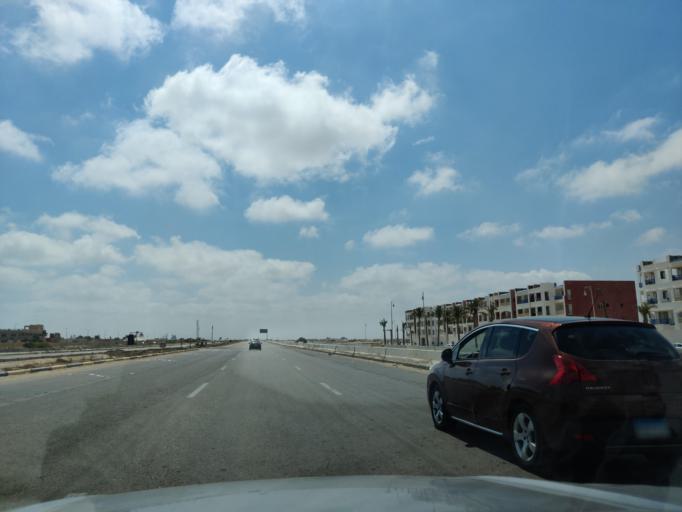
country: EG
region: Muhafazat Matruh
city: Al `Alamayn
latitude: 30.8170
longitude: 29.0304
